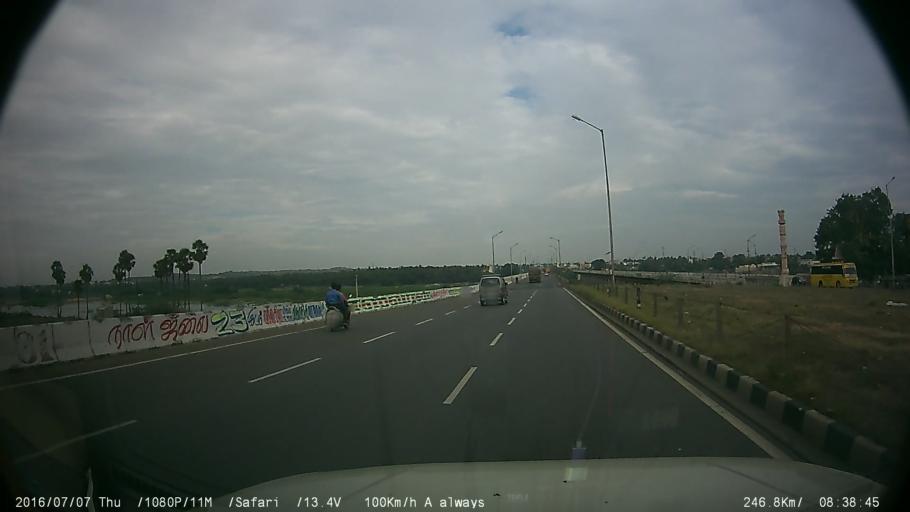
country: IN
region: Tamil Nadu
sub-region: Erode
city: Bhavani
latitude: 11.4308
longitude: 77.6887
